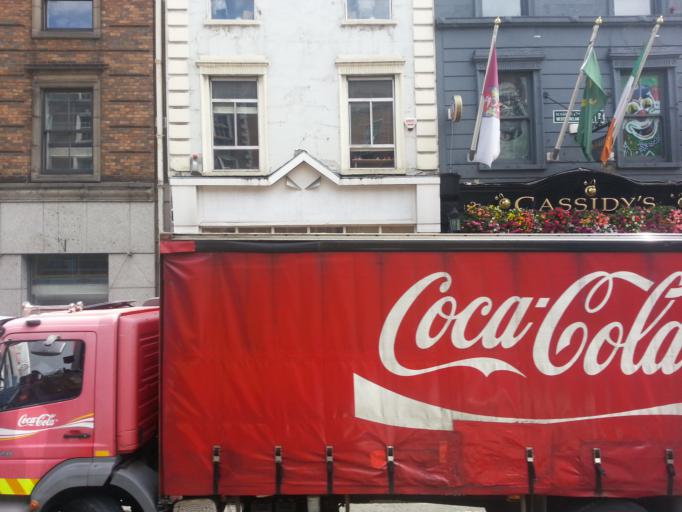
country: IE
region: Leinster
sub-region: Dublin City
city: Dublin
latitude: 53.3464
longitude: -6.2591
